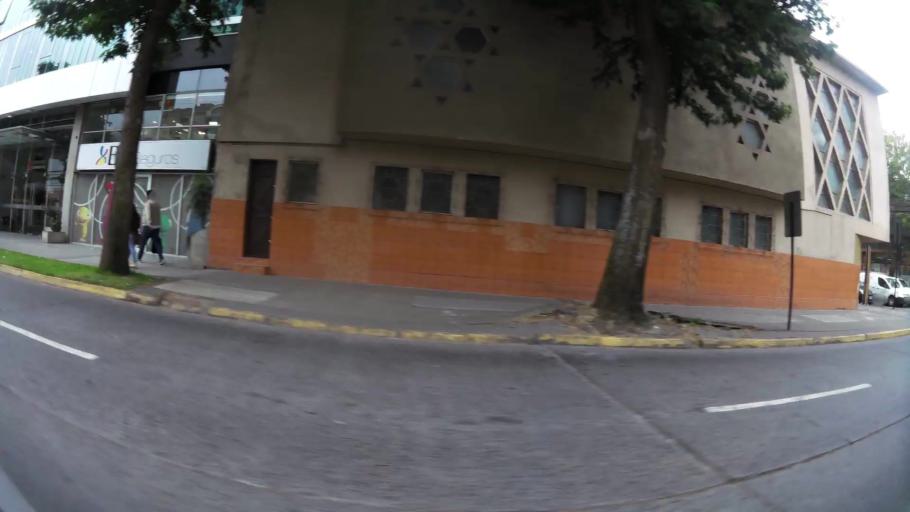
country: CL
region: Biobio
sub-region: Provincia de Concepcion
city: Concepcion
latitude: -36.8315
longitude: -73.0502
